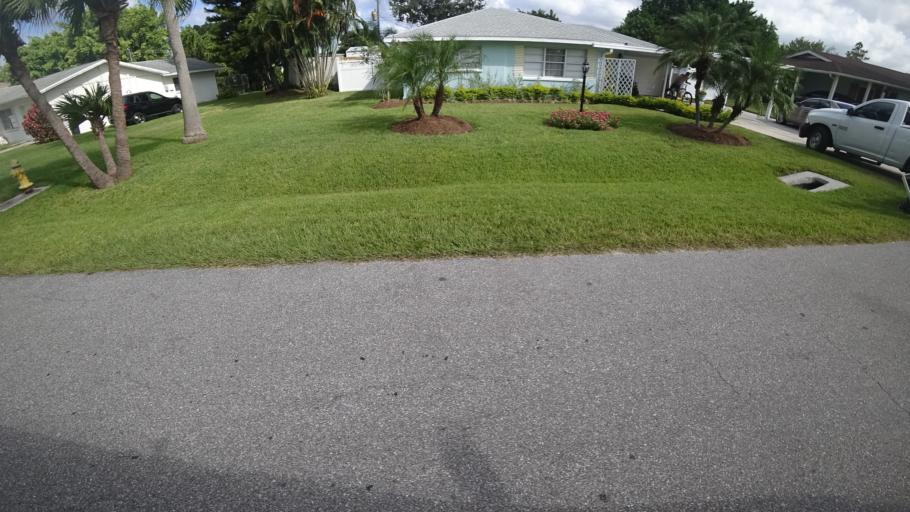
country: US
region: Florida
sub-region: Manatee County
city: Memphis
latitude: 27.5532
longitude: -82.5704
